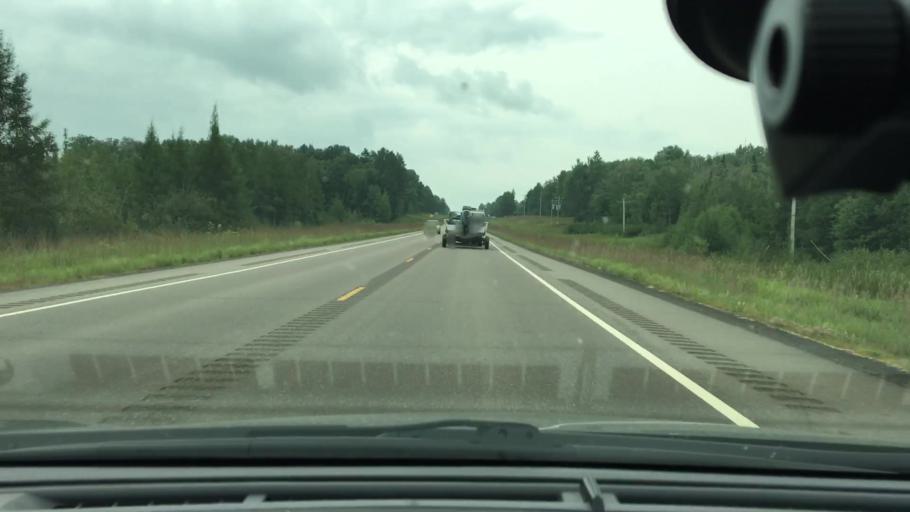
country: US
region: Minnesota
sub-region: Crow Wing County
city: Crosby
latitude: 46.5989
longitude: -93.9527
